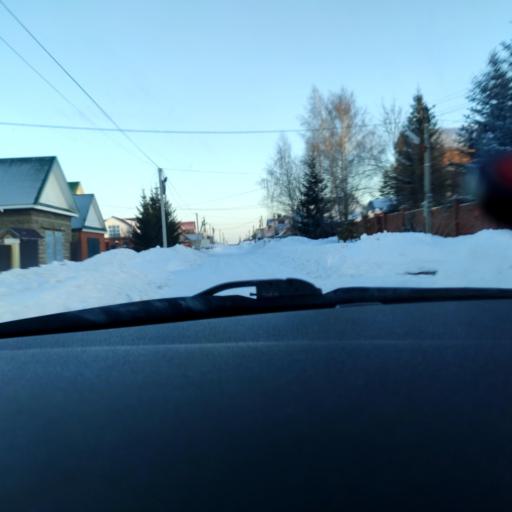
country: RU
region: Bashkortostan
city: Kabakovo
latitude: 54.6342
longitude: 56.1016
